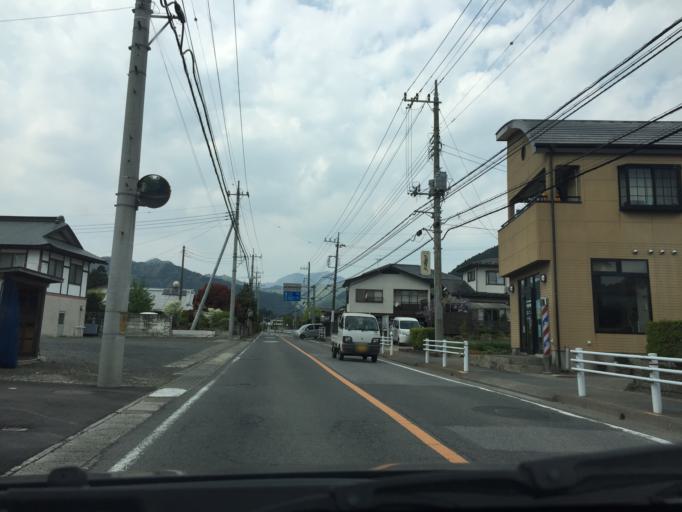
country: JP
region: Tochigi
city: Imaichi
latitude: 36.7828
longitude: 139.7110
